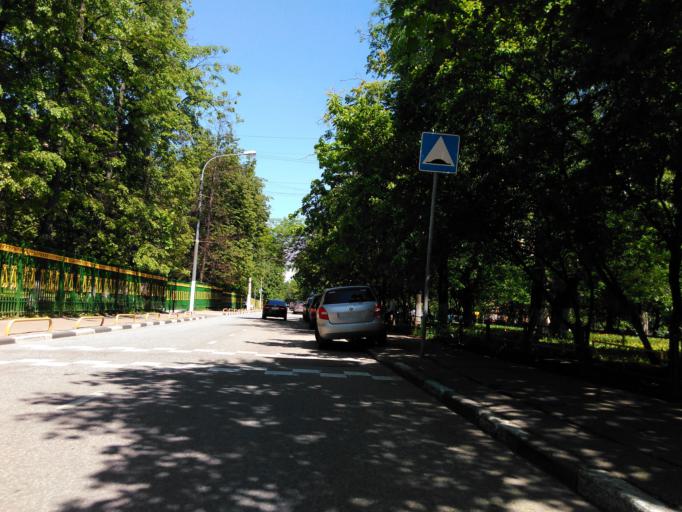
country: RU
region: Moskovskaya
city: Semenovskoye
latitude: 55.6938
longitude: 37.5507
